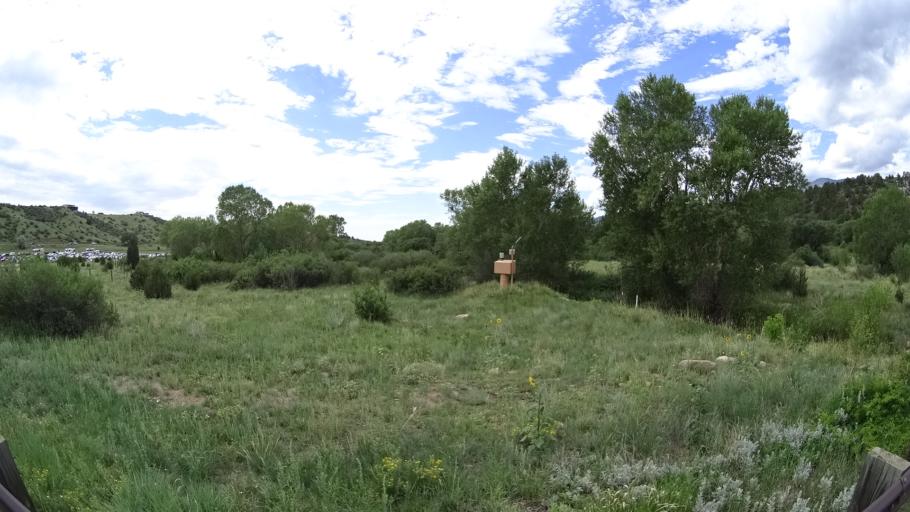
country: US
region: Colorado
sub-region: El Paso County
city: Manitou Springs
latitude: 38.8773
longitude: -104.8728
